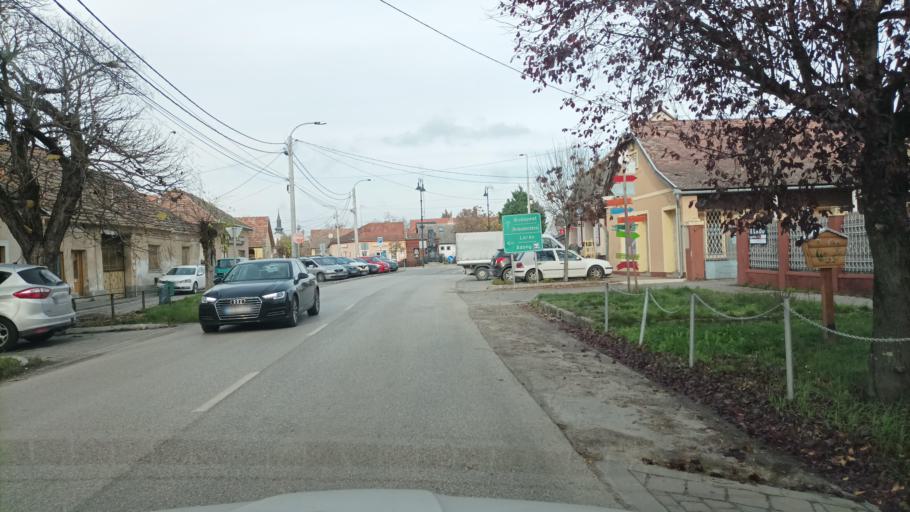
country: HU
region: Pest
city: Rackeve
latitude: 47.1562
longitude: 18.9449
